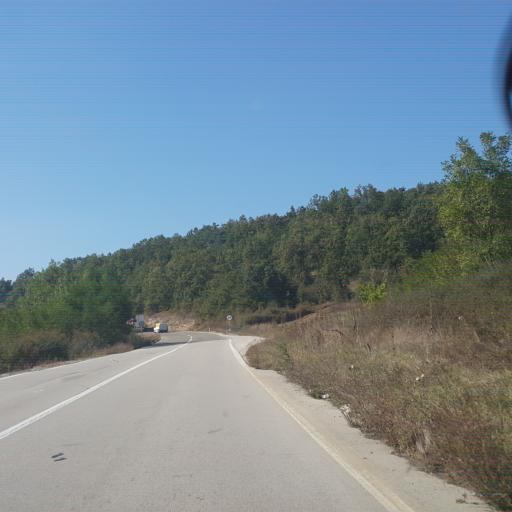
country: RS
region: Central Serbia
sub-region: Nisavski Okrug
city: Svrljig
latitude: 43.4547
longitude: 22.1837
